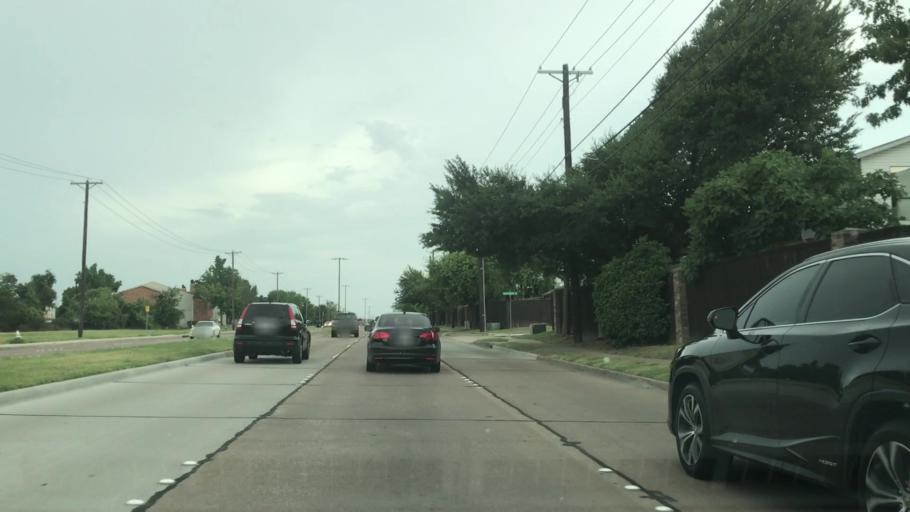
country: US
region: Texas
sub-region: Dallas County
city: Rowlett
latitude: 32.8540
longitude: -96.6003
